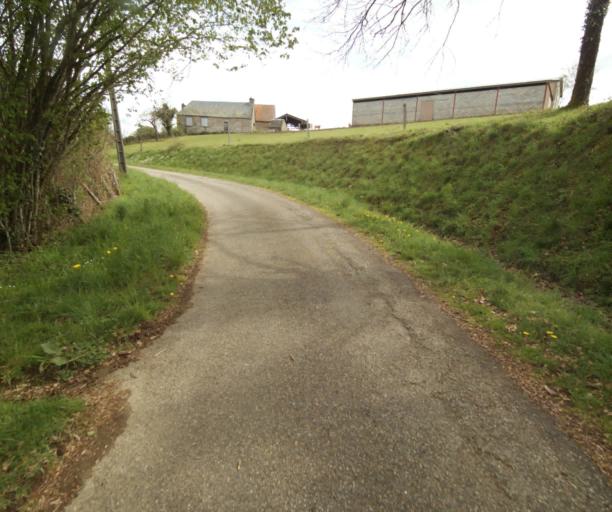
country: FR
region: Limousin
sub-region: Departement de la Correze
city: Laguenne
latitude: 45.2211
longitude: 1.8459
